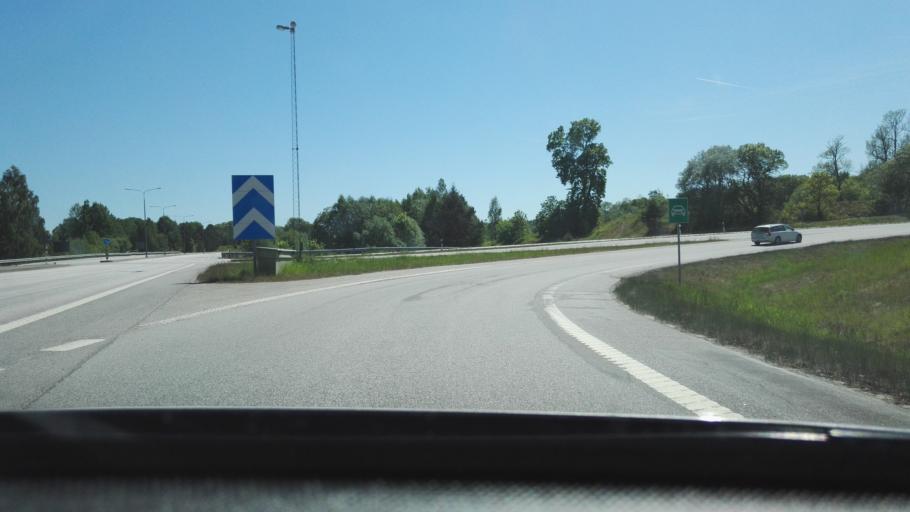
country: SE
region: Blekinge
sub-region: Ronneby Kommun
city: Kallinge
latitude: 56.2292
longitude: 15.2610
